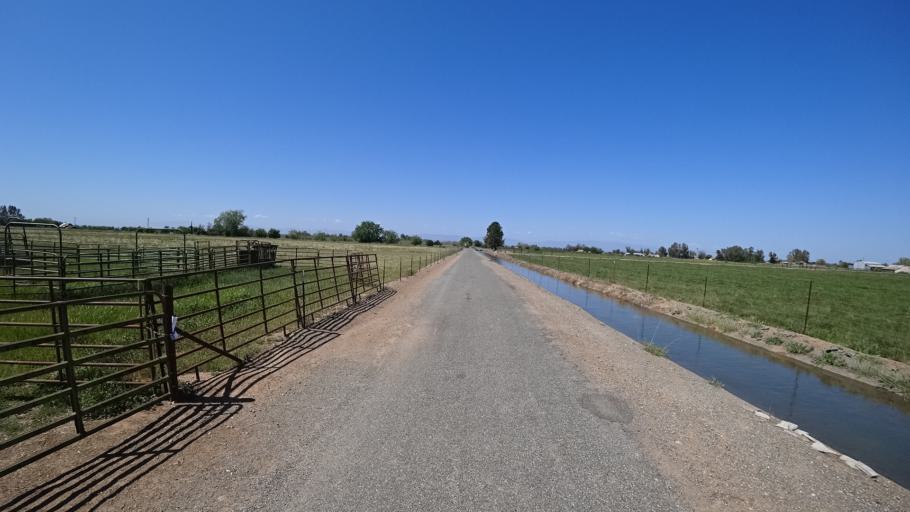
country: US
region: California
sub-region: Glenn County
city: Orland
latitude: 39.7835
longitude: -122.1808
